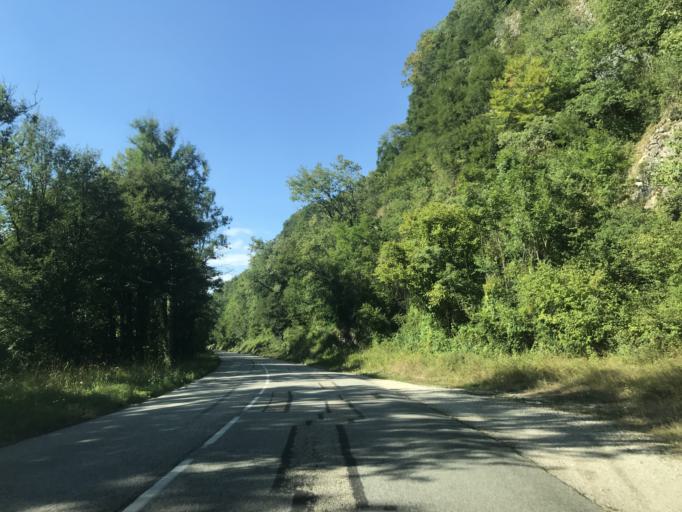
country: FR
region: Rhone-Alpes
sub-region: Departement de la Savoie
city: Chatillon
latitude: 45.7720
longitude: 5.7839
